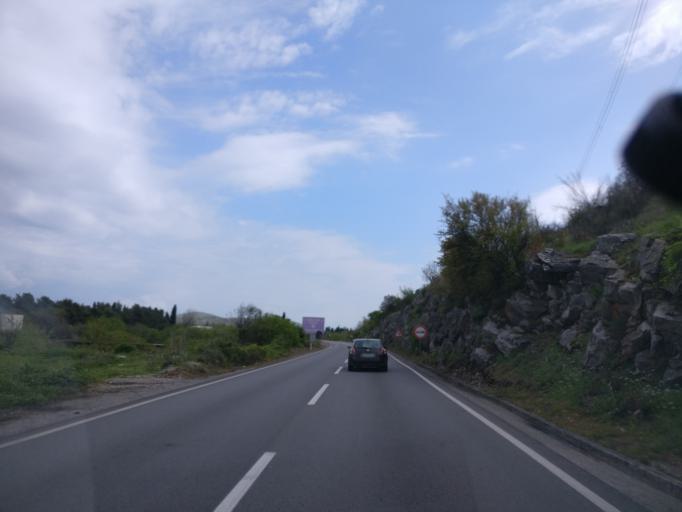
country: ME
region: Podgorica
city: Podgorica
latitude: 42.4462
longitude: 19.2024
